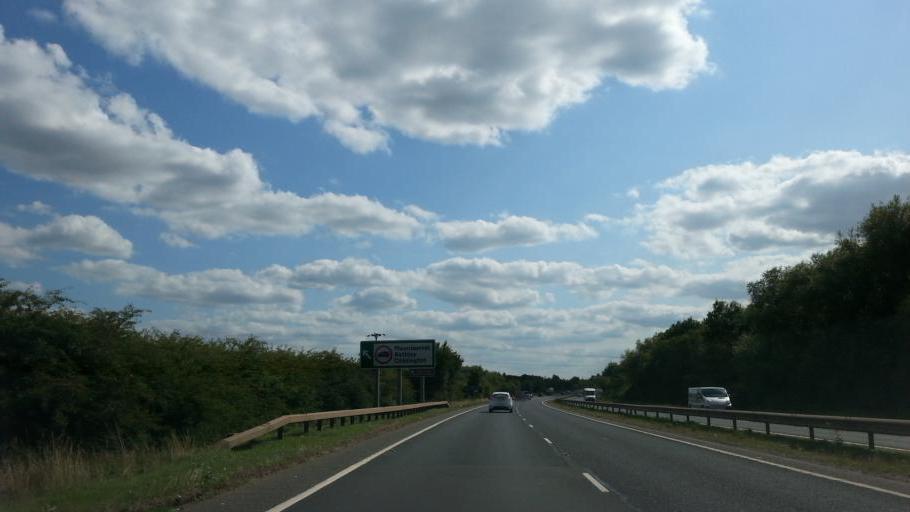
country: GB
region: England
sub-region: Leicestershire
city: Mountsorrel
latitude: 52.7284
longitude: -1.1312
